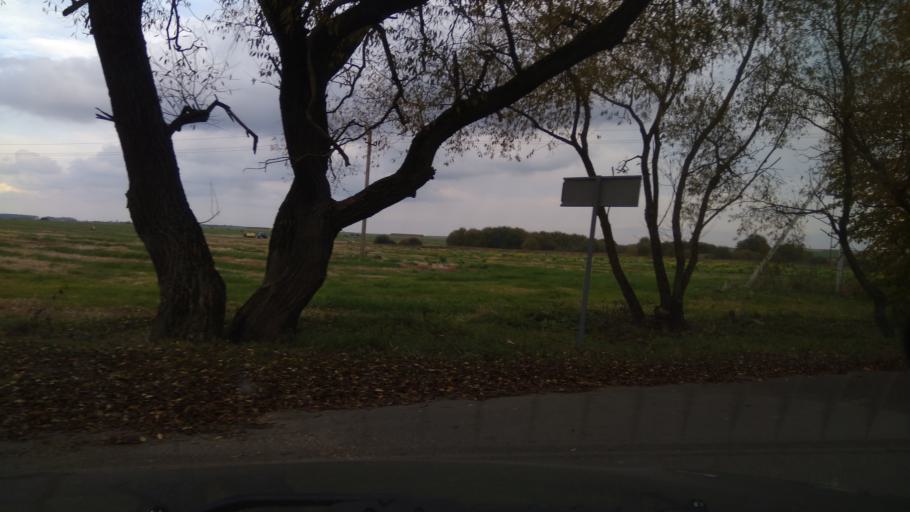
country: BY
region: Minsk
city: Dukora
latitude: 53.6815
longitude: 27.9566
